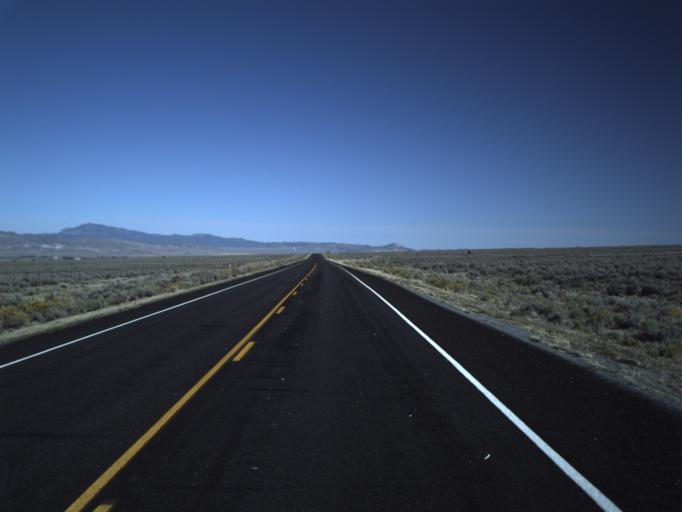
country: US
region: Utah
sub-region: Beaver County
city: Milford
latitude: 38.2402
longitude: -112.9384
